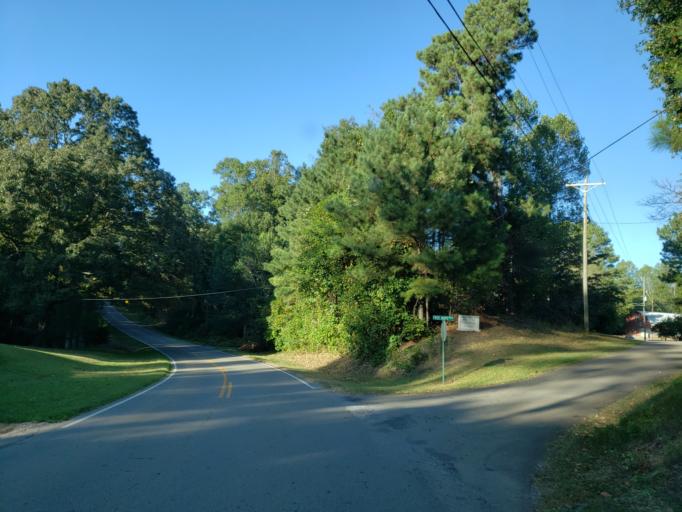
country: US
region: Georgia
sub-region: Pickens County
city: Nelson
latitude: 34.3963
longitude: -84.3999
